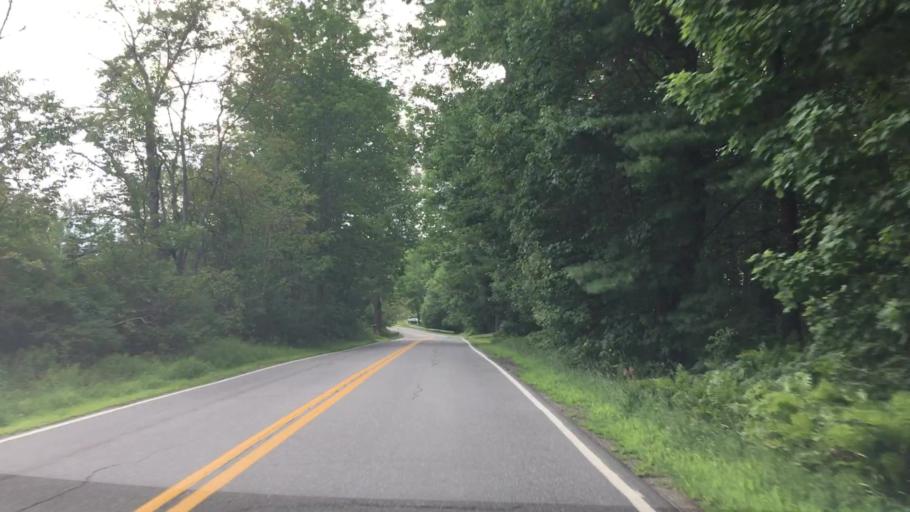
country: US
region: Maine
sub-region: Knox County
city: Hope
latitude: 44.3073
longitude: -69.0925
